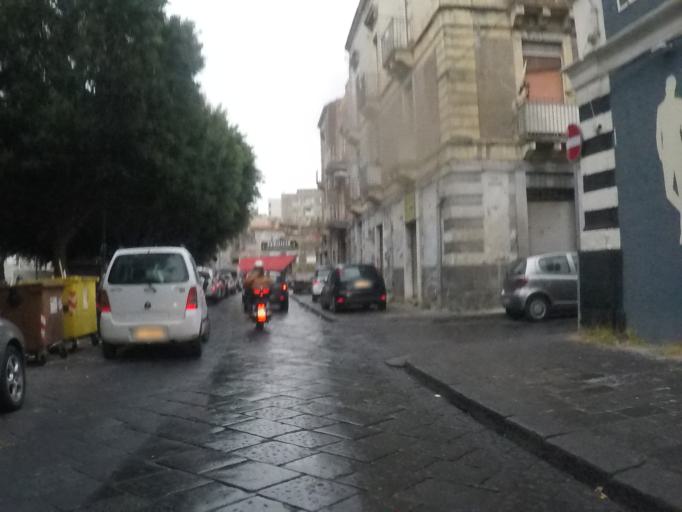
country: IT
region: Sicily
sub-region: Catania
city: Catania
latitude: 37.4999
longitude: 15.0732
